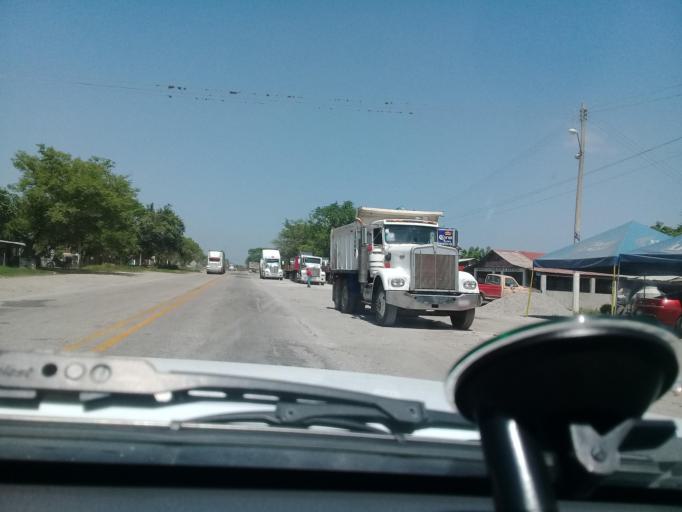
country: MX
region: Veracruz
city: Moralillo
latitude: 22.1716
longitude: -98.0502
